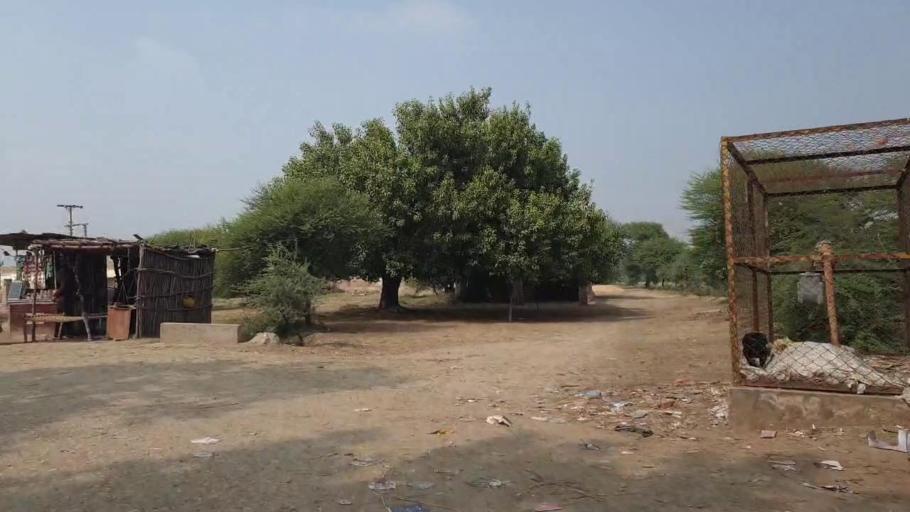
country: PK
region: Sindh
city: Kario
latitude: 24.8787
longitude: 68.5130
